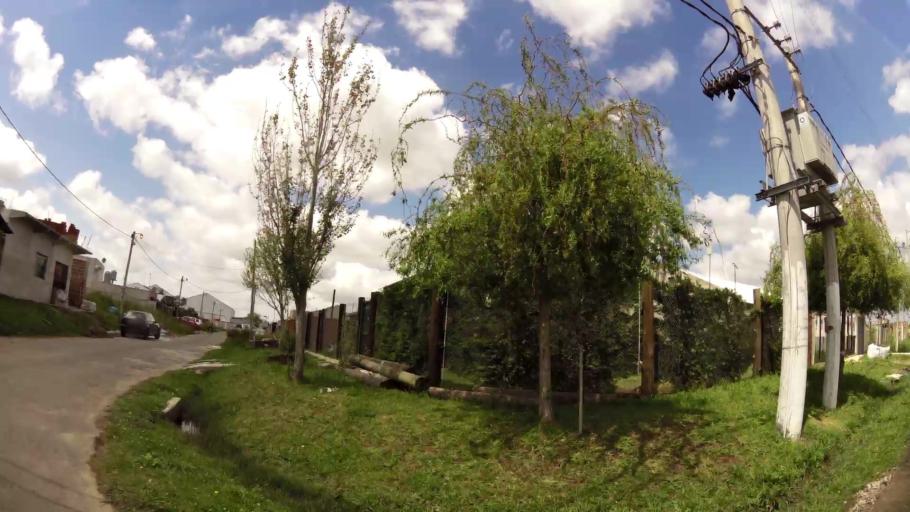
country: AR
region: Buenos Aires
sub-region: Partido de Quilmes
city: Quilmes
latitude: -34.8320
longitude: -58.2399
